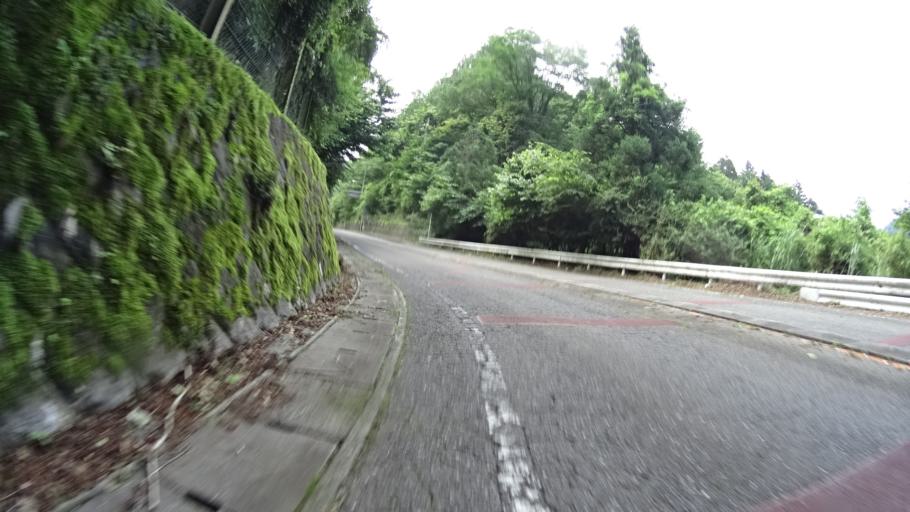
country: JP
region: Kanagawa
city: Hadano
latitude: 35.5014
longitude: 139.2313
